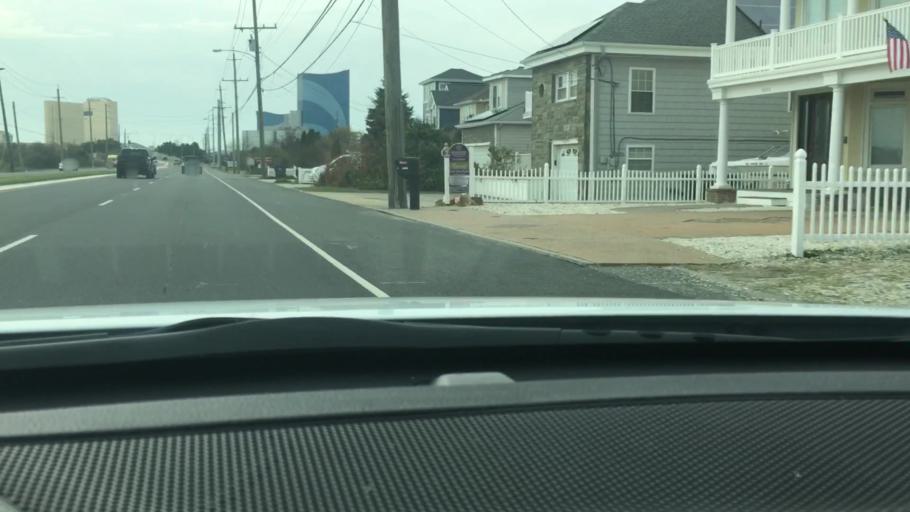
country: US
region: New Jersey
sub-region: Atlantic County
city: Atlantic City
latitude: 39.3901
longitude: -74.4135
